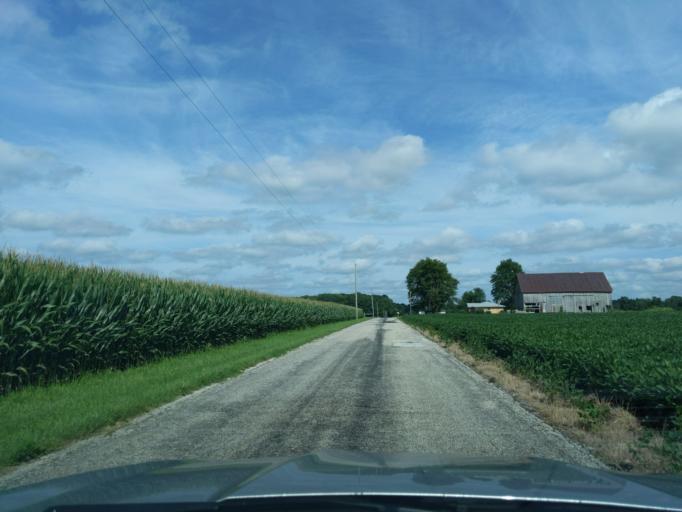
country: US
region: Indiana
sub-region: Decatur County
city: Greensburg
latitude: 39.2348
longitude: -85.4098
